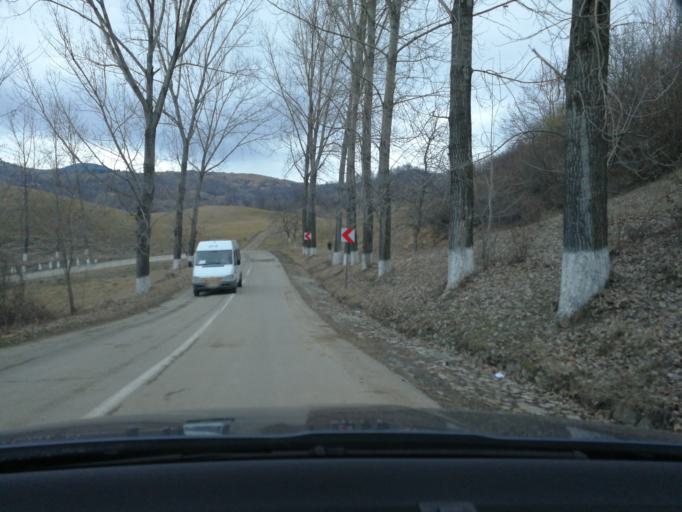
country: RO
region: Prahova
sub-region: Oras Breaza
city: Valea Tarsei
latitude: 45.1839
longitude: 25.6150
